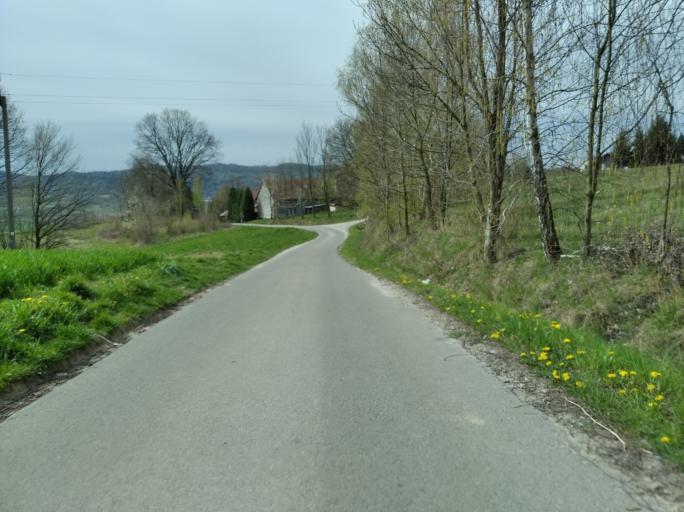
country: PL
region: Subcarpathian Voivodeship
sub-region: Powiat strzyzowski
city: Wisniowa
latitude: 49.8789
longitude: 21.6696
